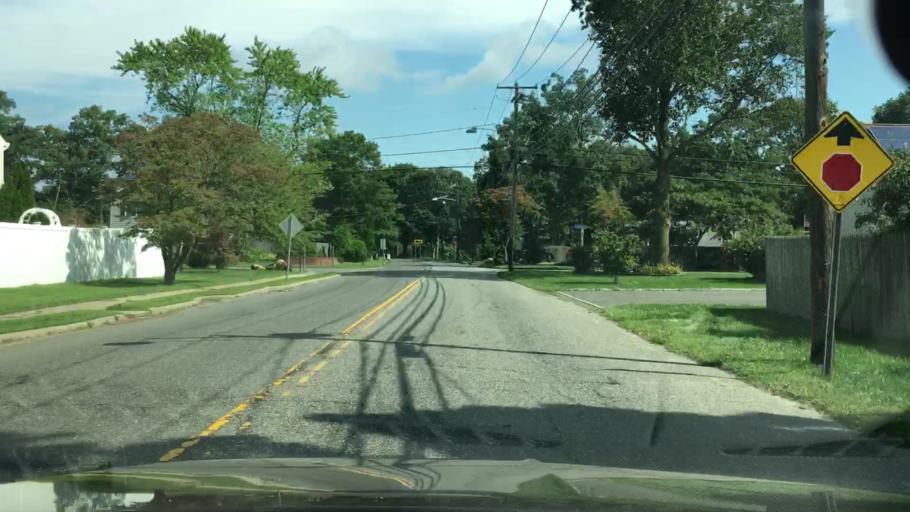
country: US
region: New York
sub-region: Suffolk County
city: Ronkonkoma
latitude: 40.7995
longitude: -73.1279
